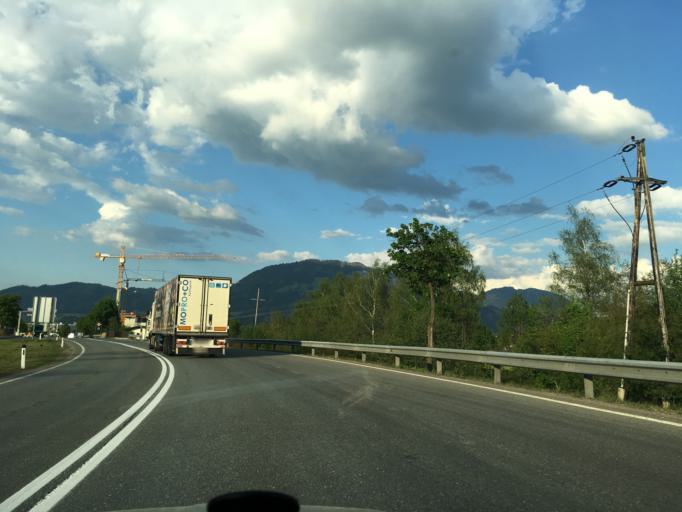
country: AT
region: Tyrol
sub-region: Politischer Bezirk Kitzbuhel
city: Sankt Johann in Tirol
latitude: 47.5169
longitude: 12.4113
